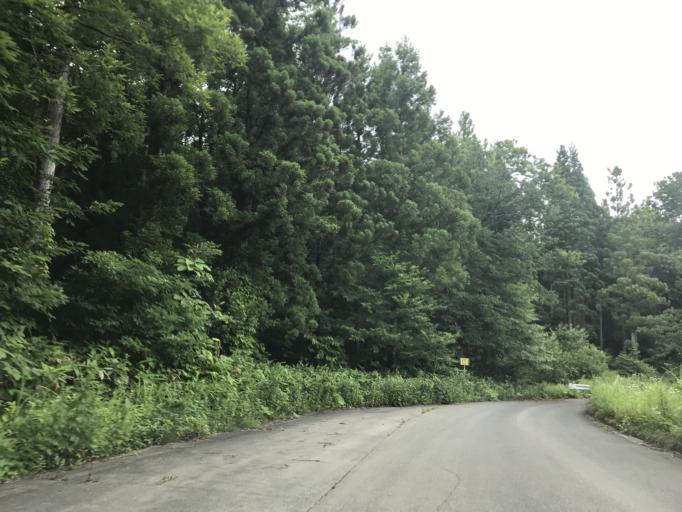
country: JP
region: Iwate
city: Ichinoseki
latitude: 38.9578
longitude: 140.8901
